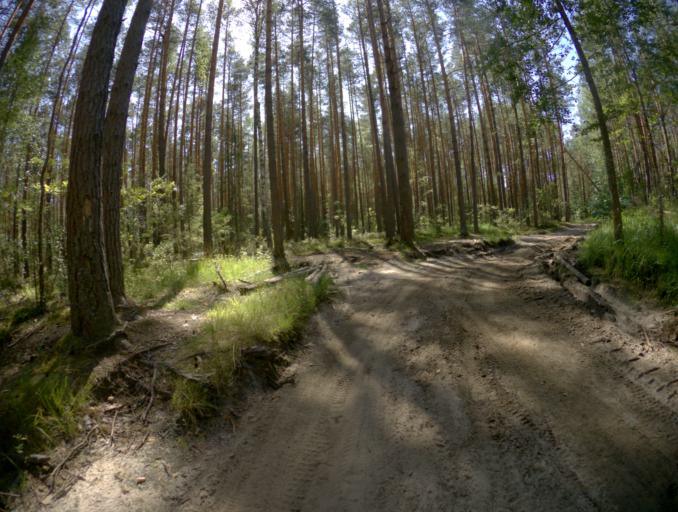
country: RU
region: Vladimir
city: Sobinka
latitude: 55.9474
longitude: 39.9939
